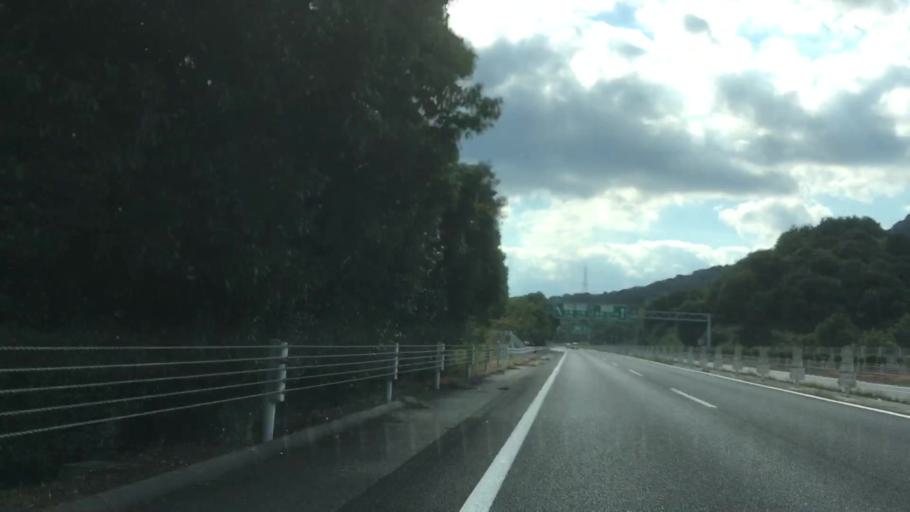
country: JP
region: Hiroshima
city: Hatsukaichi
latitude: 34.3398
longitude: 132.2999
